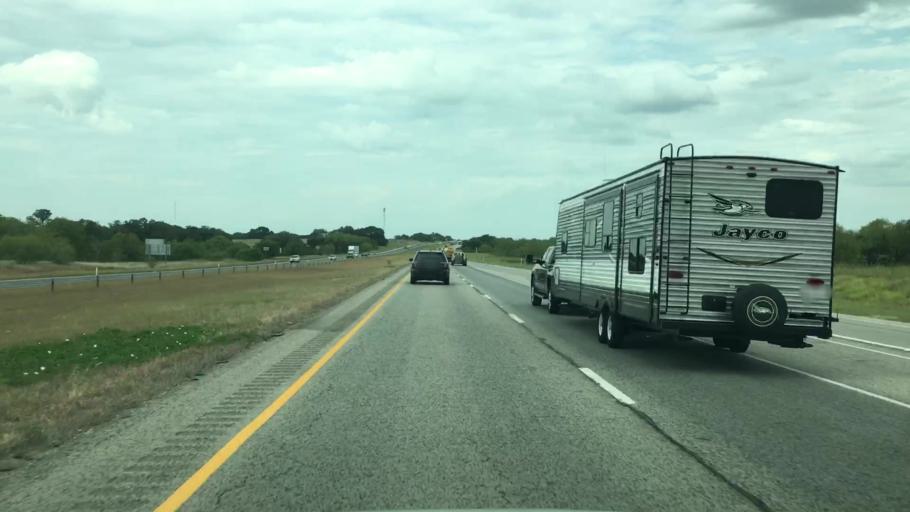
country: US
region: Texas
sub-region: Atascosa County
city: Pleasanton
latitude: 29.1103
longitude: -98.4321
